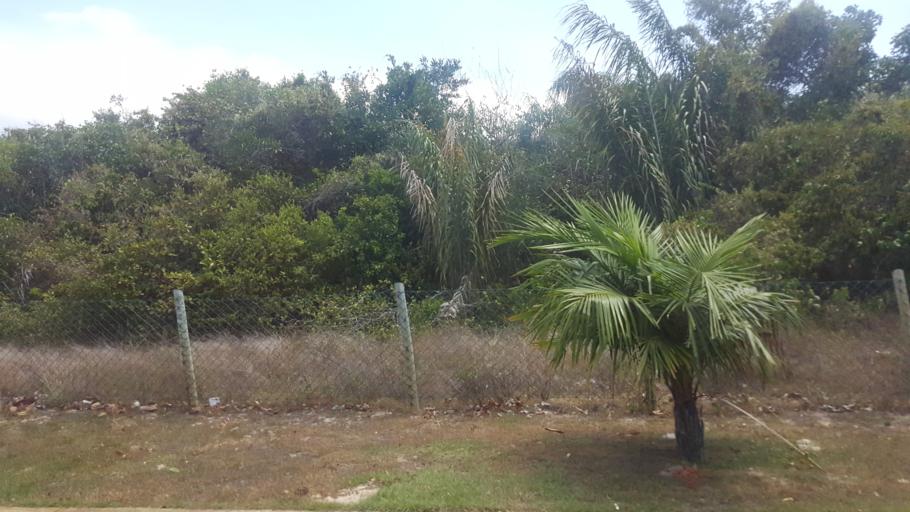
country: BR
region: Bahia
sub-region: Mata De Sao Joao
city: Mata de Sao Joao
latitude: -12.4811
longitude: -37.9592
